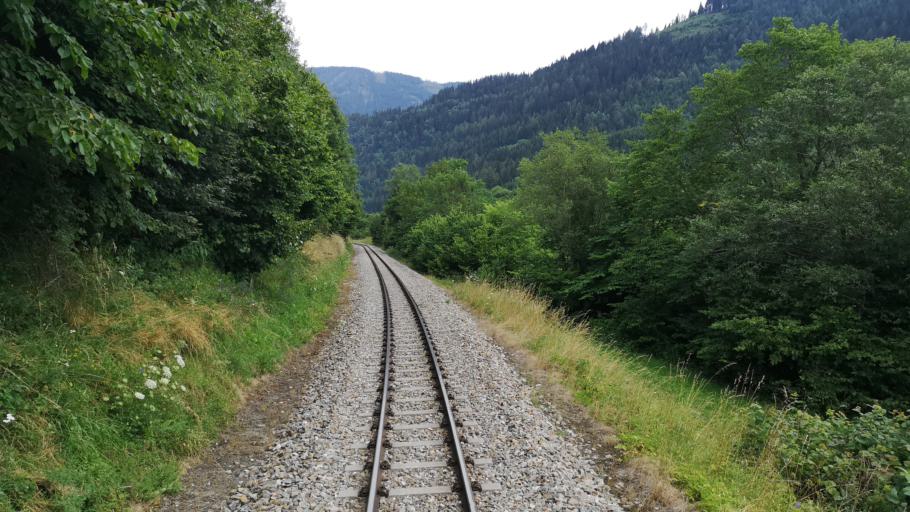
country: AT
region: Salzburg
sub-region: Politischer Bezirk Tamsweg
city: Ramingstein
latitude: 47.0669
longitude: 13.8907
